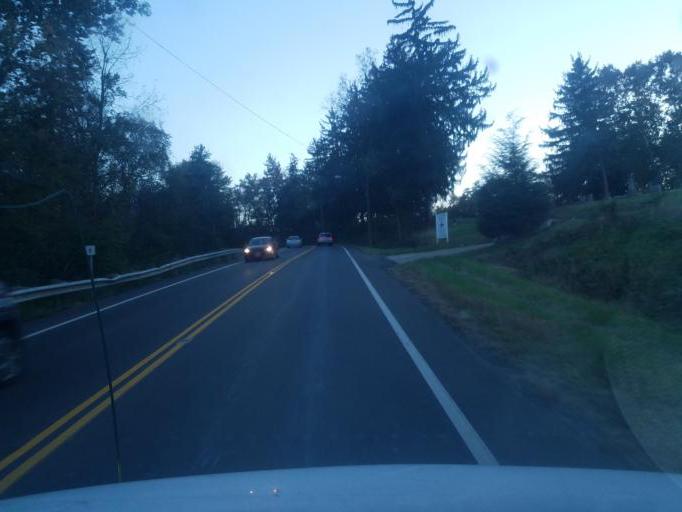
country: US
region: Ohio
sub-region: Licking County
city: Newark
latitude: 40.0353
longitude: -82.4027
